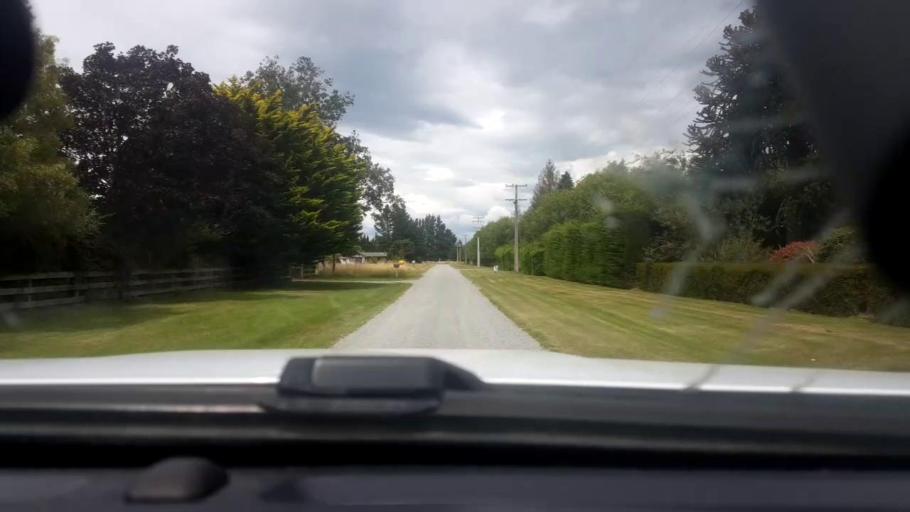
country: NZ
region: Canterbury
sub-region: Timaru District
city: Pleasant Point
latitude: -44.1424
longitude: 171.2894
